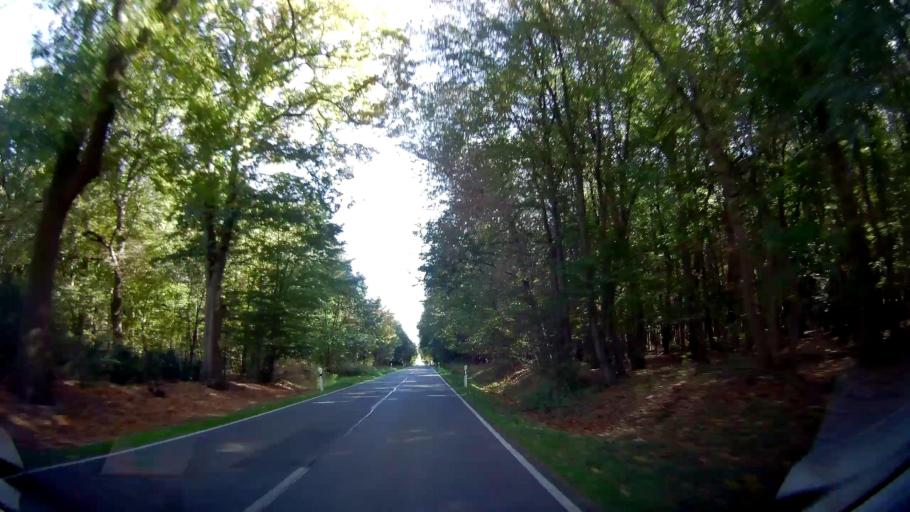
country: DE
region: North Rhine-Westphalia
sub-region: Regierungsbezirk Dusseldorf
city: Hunxe
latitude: 51.6231
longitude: 6.7858
